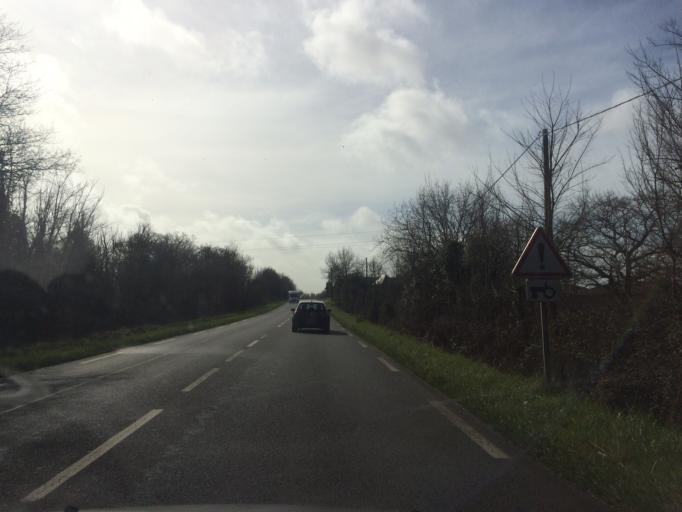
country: FR
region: Pays de la Loire
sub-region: Departement de la Loire-Atlantique
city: Besne
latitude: 47.3720
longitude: -2.0985
